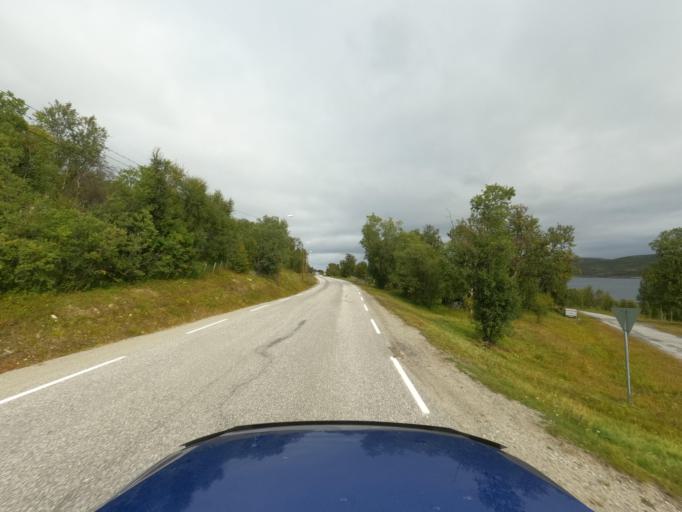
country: NO
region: Finnmark Fylke
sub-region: Porsanger
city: Lakselv
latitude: 70.3225
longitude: 25.0569
